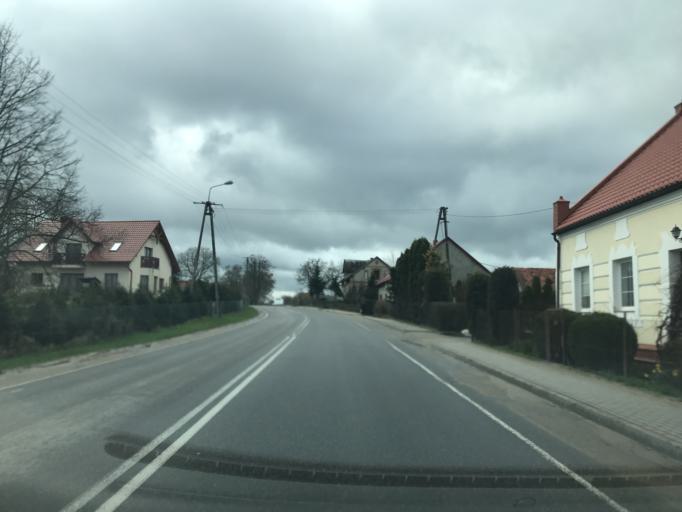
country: PL
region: Warmian-Masurian Voivodeship
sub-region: Powiat olsztynski
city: Olsztynek
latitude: 53.5328
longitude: 20.2661
